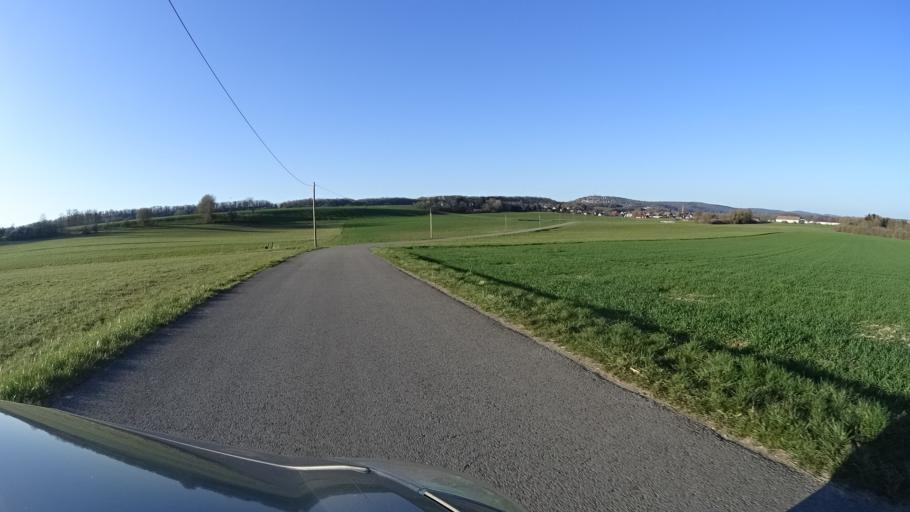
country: FR
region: Franche-Comte
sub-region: Departement du Doubs
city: Morre
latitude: 47.2004
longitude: 6.0612
